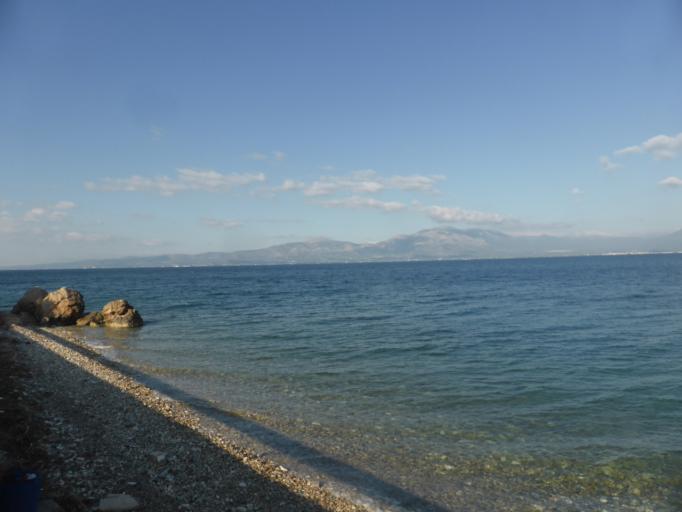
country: GR
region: Attica
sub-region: Nomarchia Anatolikis Attikis
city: Markopoulo Oropou
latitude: 38.3117
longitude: 23.8415
